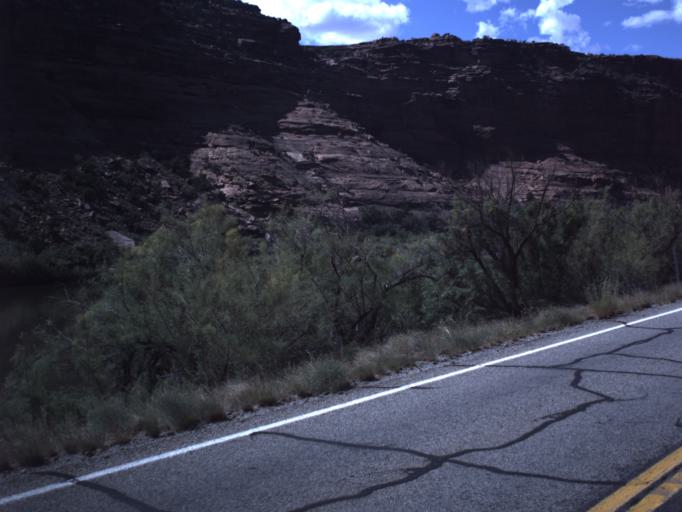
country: US
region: Utah
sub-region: Grand County
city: Moab
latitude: 38.5351
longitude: -109.6272
